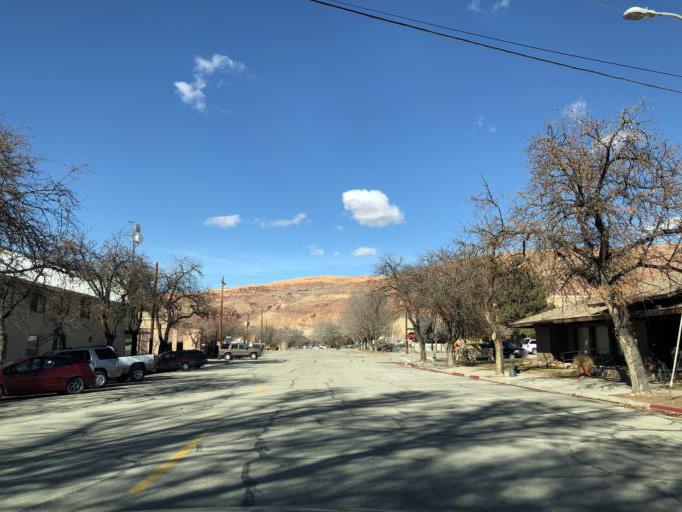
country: US
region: Utah
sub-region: Grand County
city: Moab
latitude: 38.5726
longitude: -109.5488
